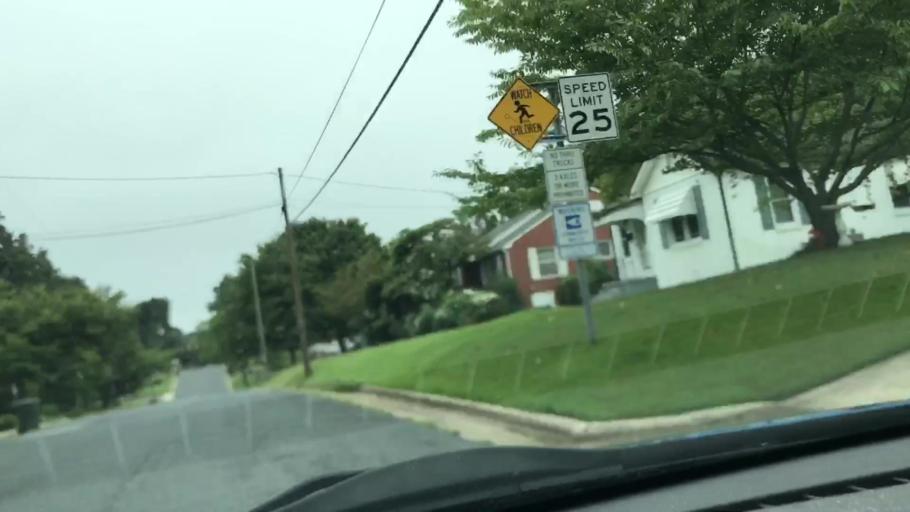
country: US
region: North Carolina
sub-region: Randolph County
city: Asheboro
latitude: 35.7171
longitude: -79.8061
